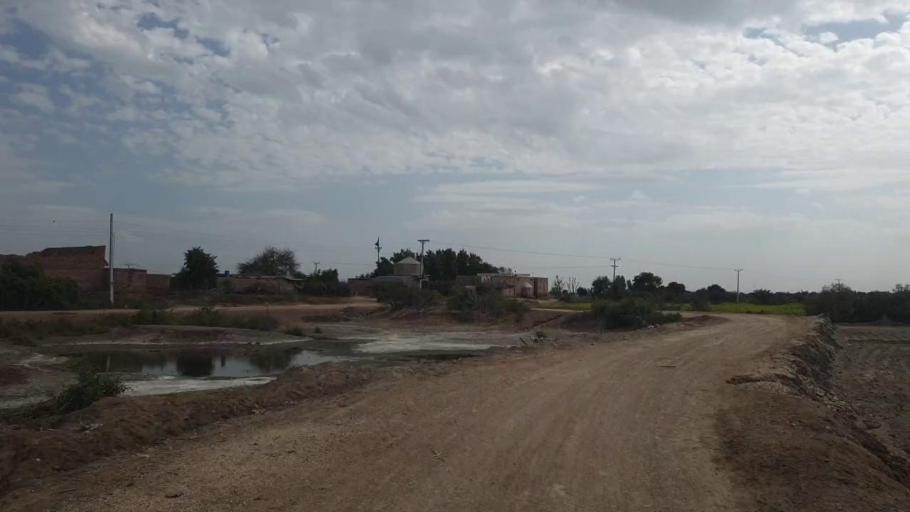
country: PK
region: Sindh
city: Hala
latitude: 25.9218
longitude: 68.4289
